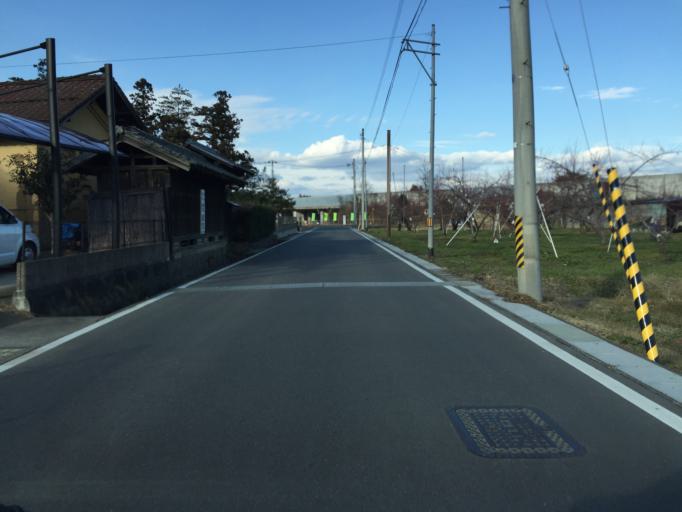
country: JP
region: Fukushima
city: Fukushima-shi
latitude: 37.7280
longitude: 140.4254
